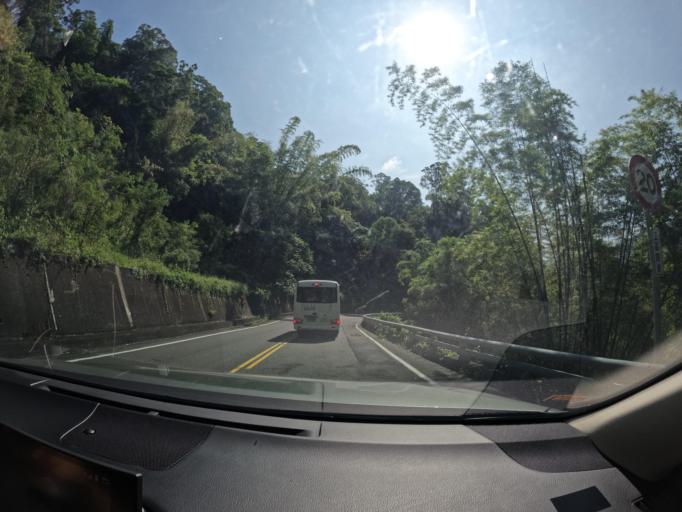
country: TW
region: Taiwan
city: Yujing
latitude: 23.0714
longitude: 120.6402
